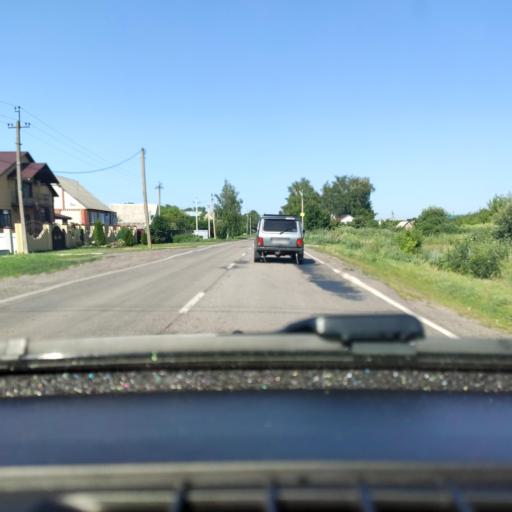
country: RU
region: Voronezj
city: Panino
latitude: 51.6527
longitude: 40.1171
